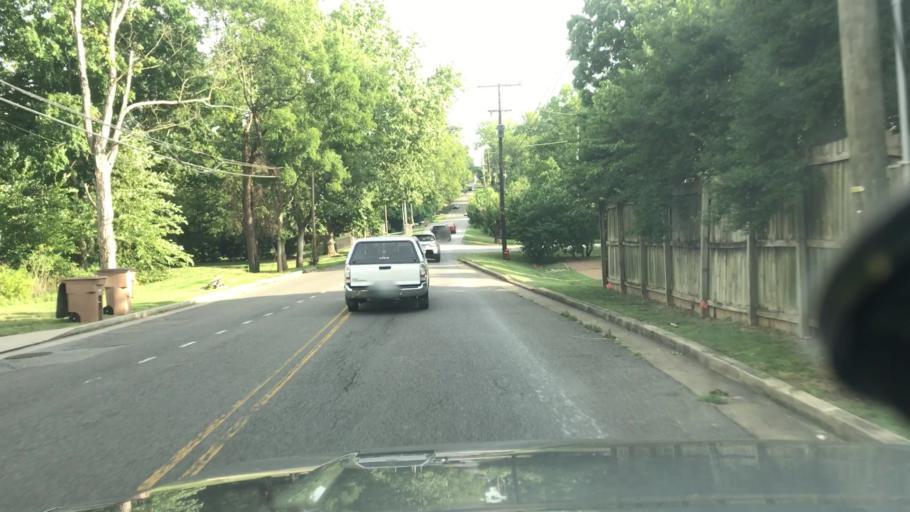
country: US
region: Tennessee
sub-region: Davidson County
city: Belle Meade
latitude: 36.1160
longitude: -86.8366
